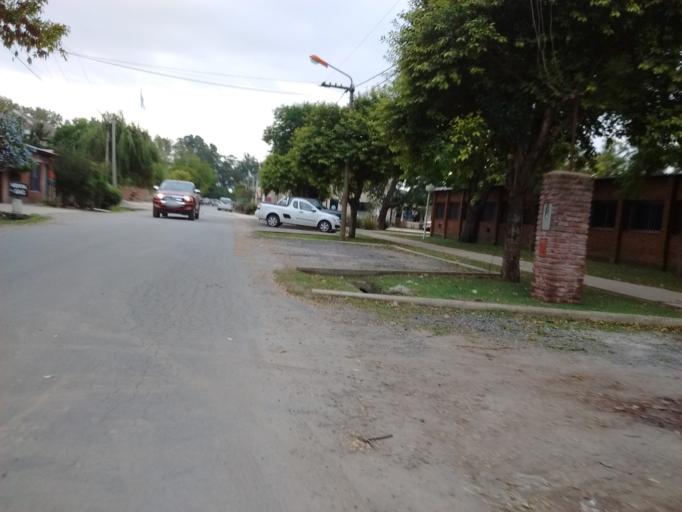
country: AR
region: Santa Fe
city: Funes
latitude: -32.8524
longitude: -60.7854
